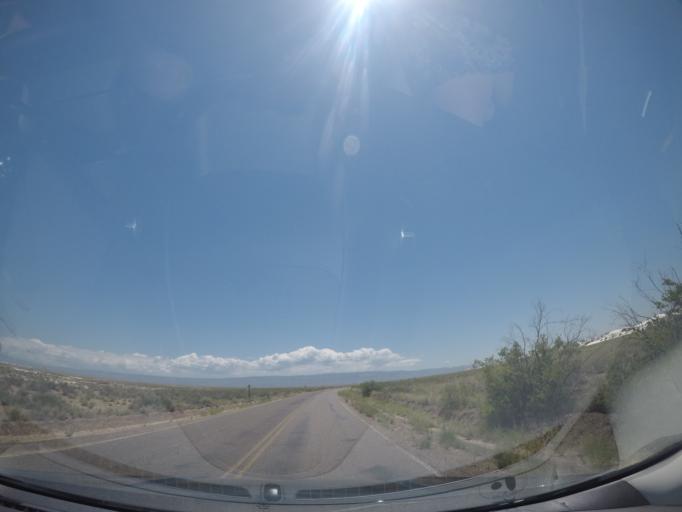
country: US
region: New Mexico
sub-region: Otero County
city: Holloman Air Force Base
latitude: 32.7956
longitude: -106.2106
